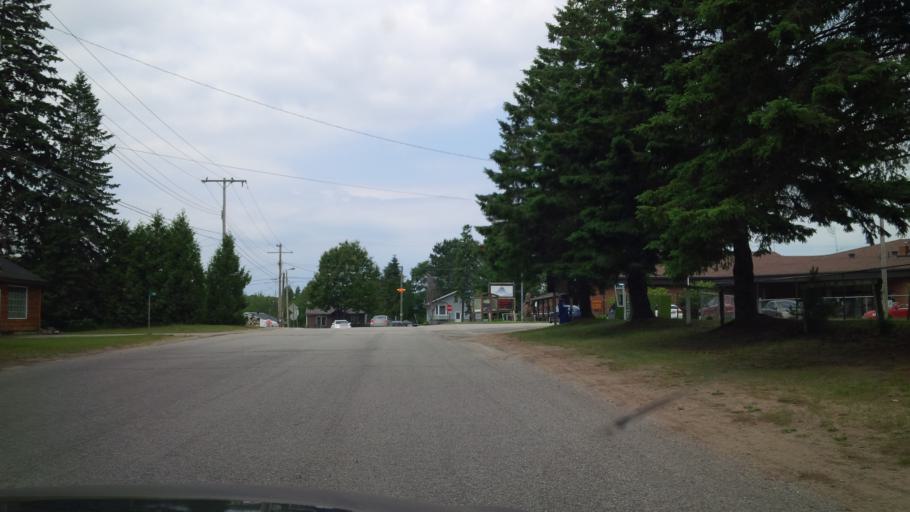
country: CA
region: Ontario
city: Huntsville
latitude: 45.5577
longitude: -79.2267
